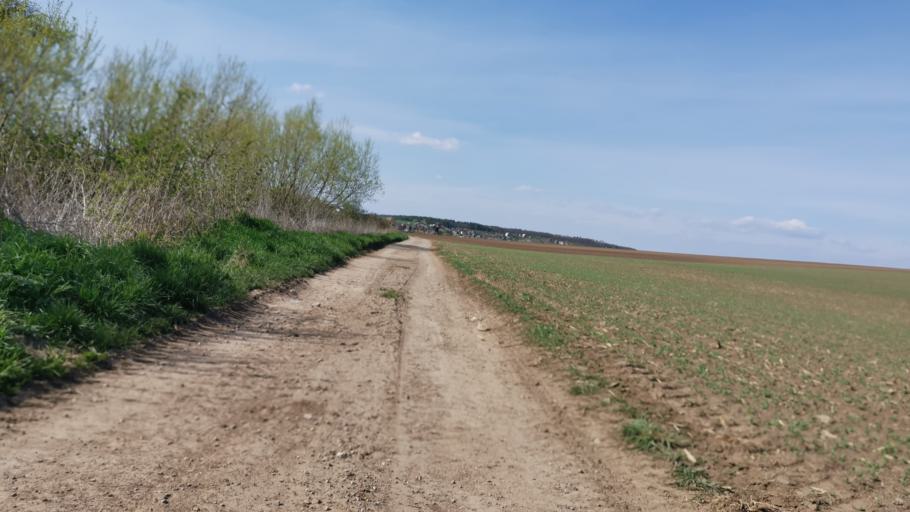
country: SK
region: Trnavsky
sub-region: Okres Skalica
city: Holic
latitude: 48.7815
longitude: 17.1782
